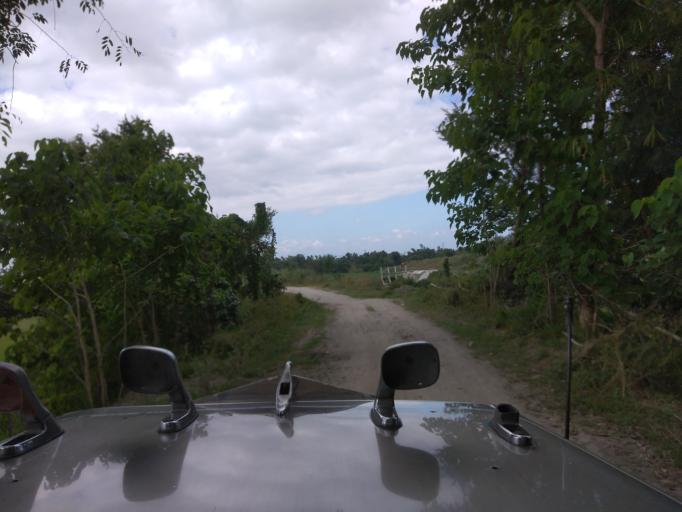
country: PH
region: Central Luzon
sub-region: Province of Pampanga
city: San Patricio
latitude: 15.1143
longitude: 120.7155
